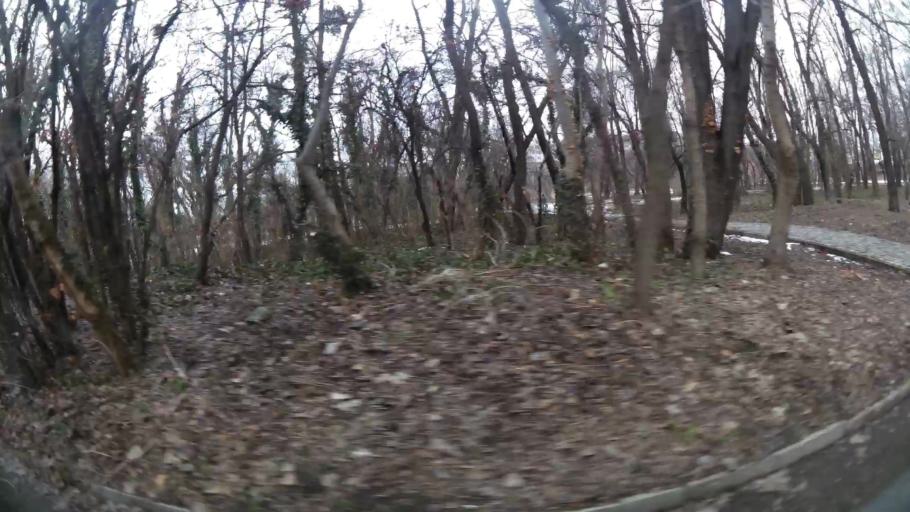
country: BG
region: Sofia-Capital
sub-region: Stolichna Obshtina
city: Sofia
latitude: 42.7223
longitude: 23.3027
